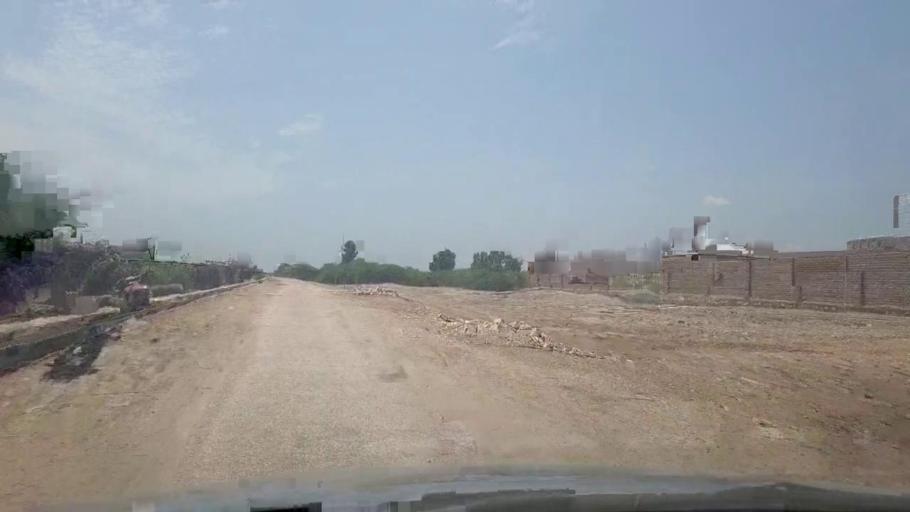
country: PK
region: Sindh
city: Kot Diji
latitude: 27.4098
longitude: 68.7335
